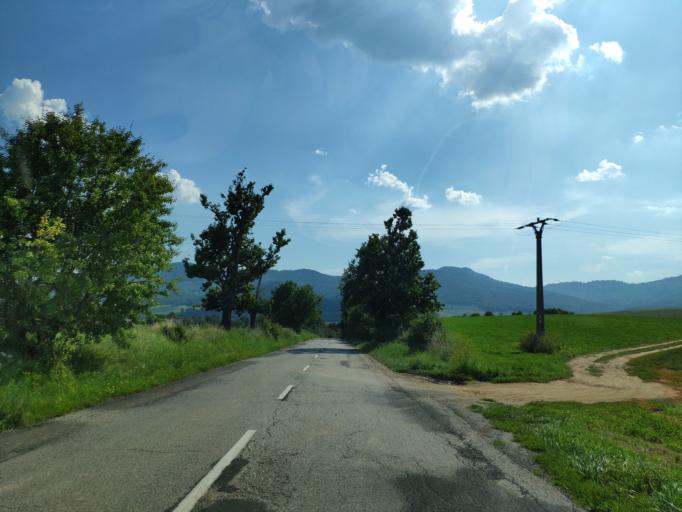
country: SK
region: Kosicky
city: Dobsina
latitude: 48.6965
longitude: 20.3529
